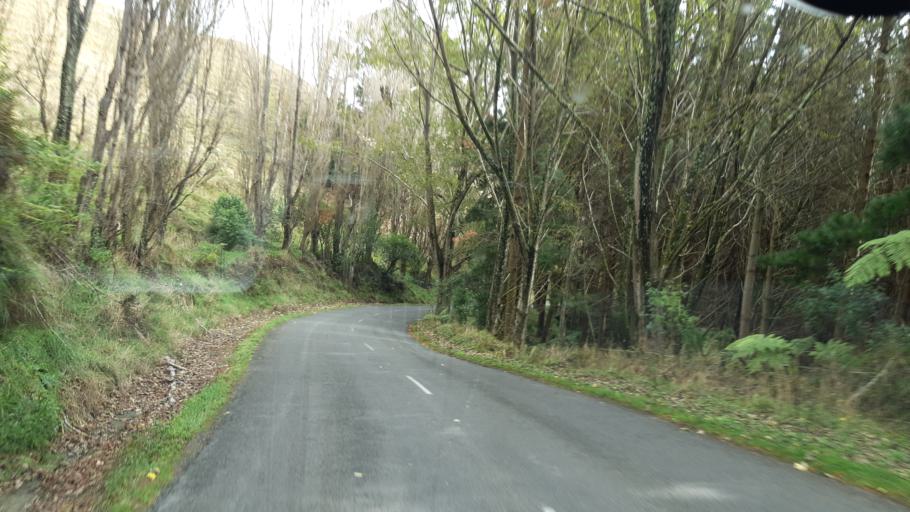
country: NZ
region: Manawatu-Wanganui
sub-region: Rangitikei District
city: Bulls
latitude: -39.9110
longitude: 175.5487
